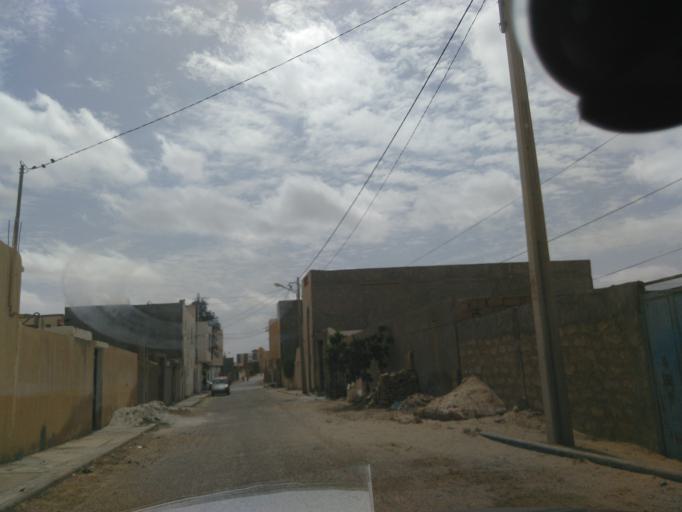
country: TN
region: Tataouine
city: Tataouine
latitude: 32.9512
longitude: 10.4653
